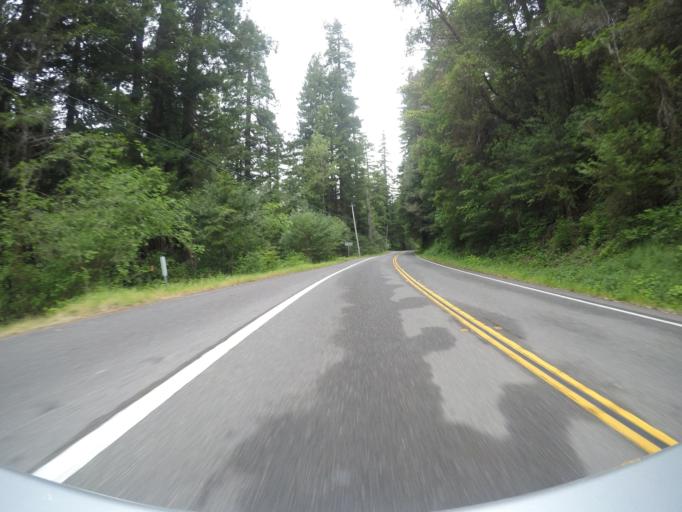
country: US
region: California
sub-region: Humboldt County
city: Rio Dell
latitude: 40.4044
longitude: -123.9516
